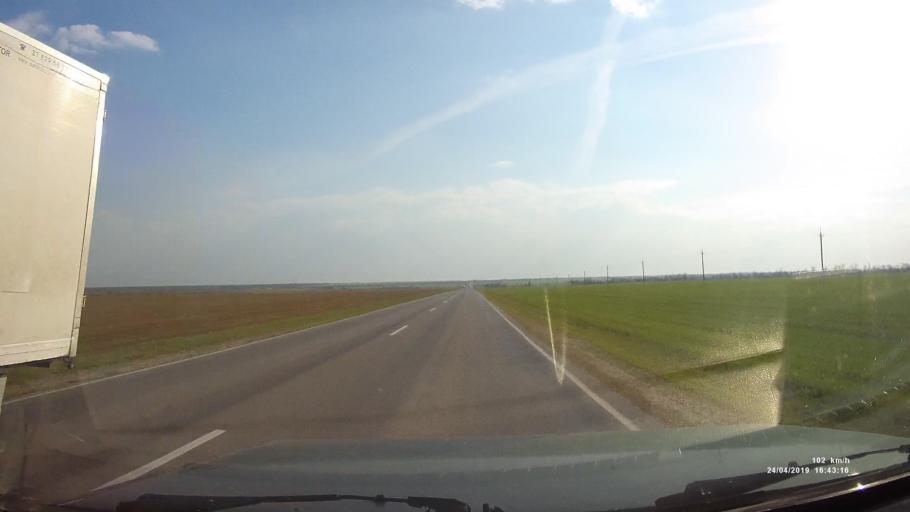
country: RU
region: Rostov
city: Gundorovskiy
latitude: 46.7965
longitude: 41.8427
